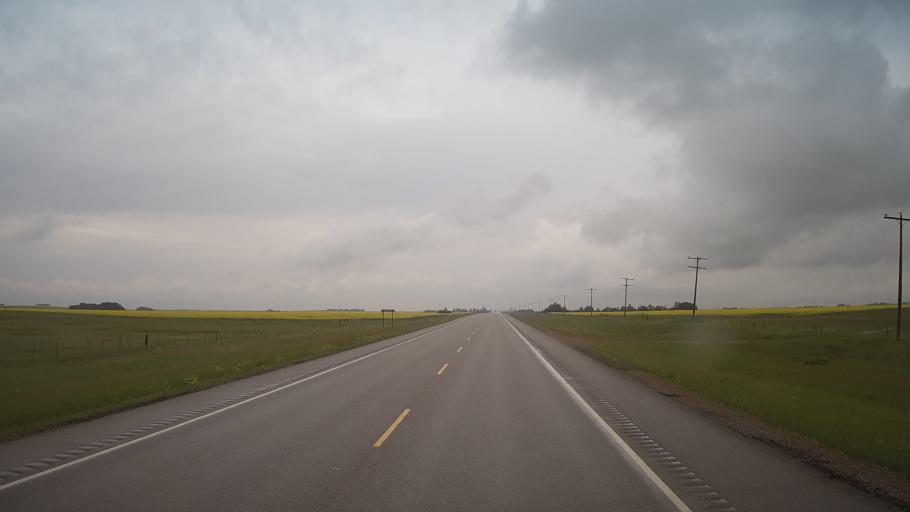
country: CA
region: Saskatchewan
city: Unity
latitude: 52.4349
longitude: -109.0034
